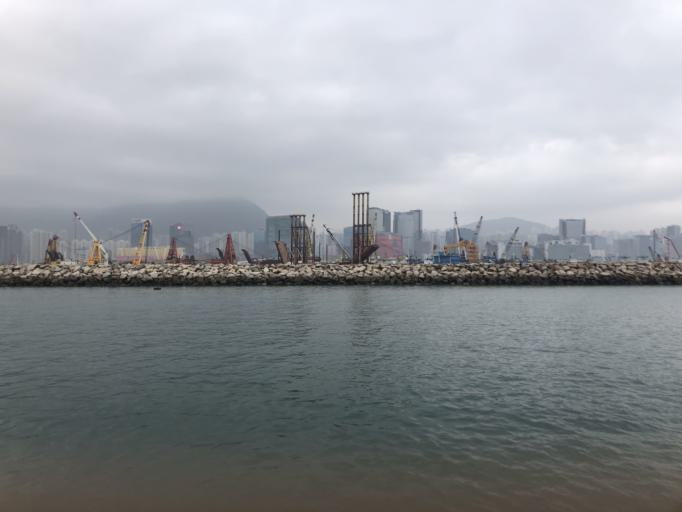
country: HK
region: Kowloon City
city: Kowloon
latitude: 22.3123
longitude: 114.1943
